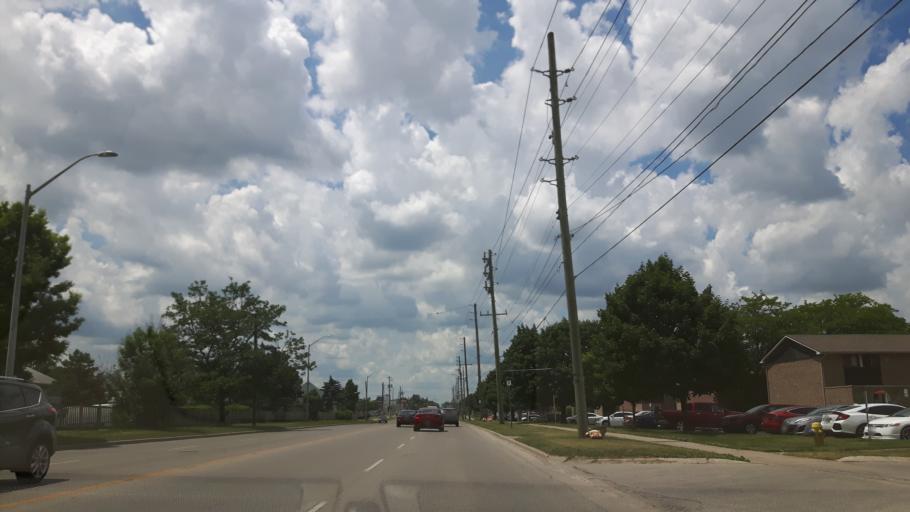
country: CA
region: Ontario
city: London
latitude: 42.9424
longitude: -81.2386
